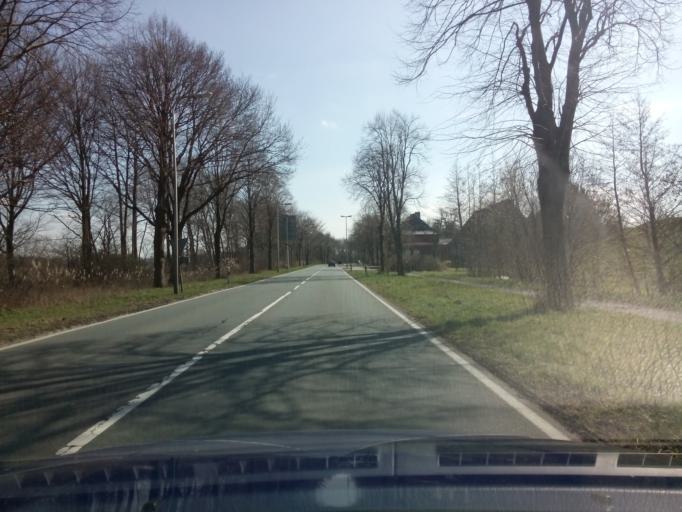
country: NL
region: Drenthe
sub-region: Gemeente Coevorden
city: Coevorden
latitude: 52.6470
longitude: 6.7558
